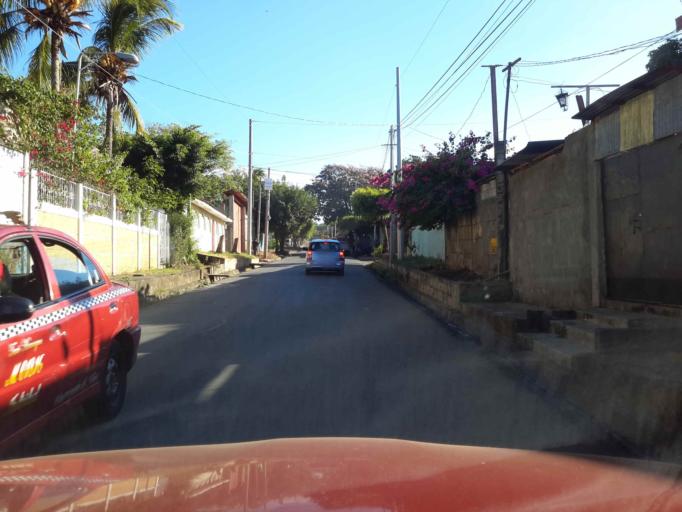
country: NI
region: Managua
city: Managua
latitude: 12.1134
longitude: -86.2935
